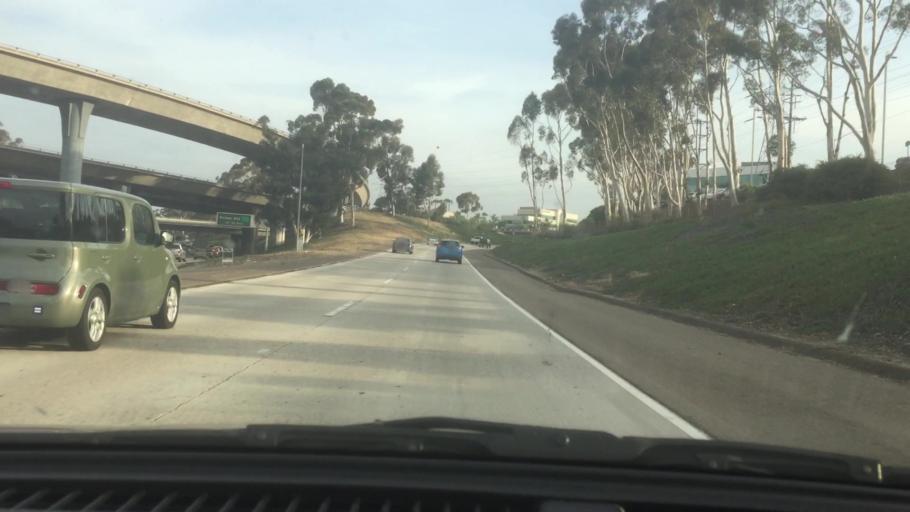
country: US
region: California
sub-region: San Diego County
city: San Diego
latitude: 32.8075
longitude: -117.1516
